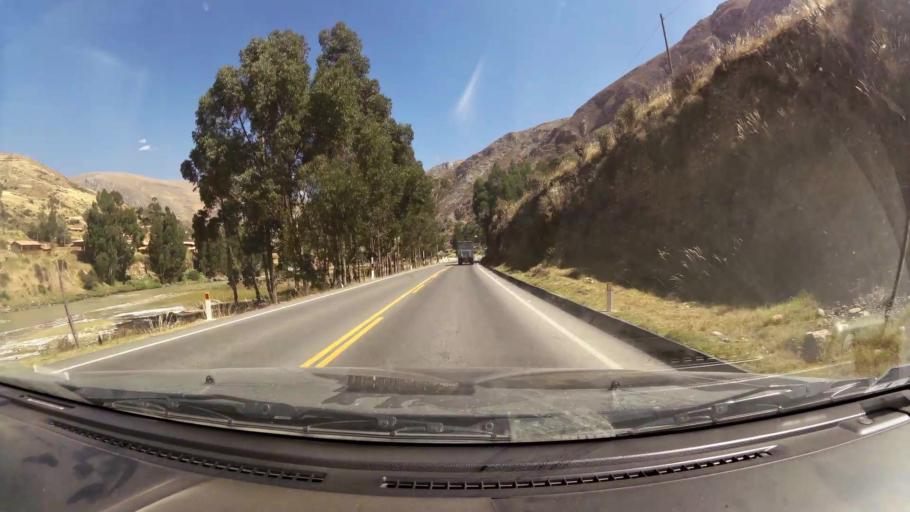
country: PE
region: Junin
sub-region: Provincia de Jauja
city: Llocllapampa
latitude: -11.7960
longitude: -75.5904
